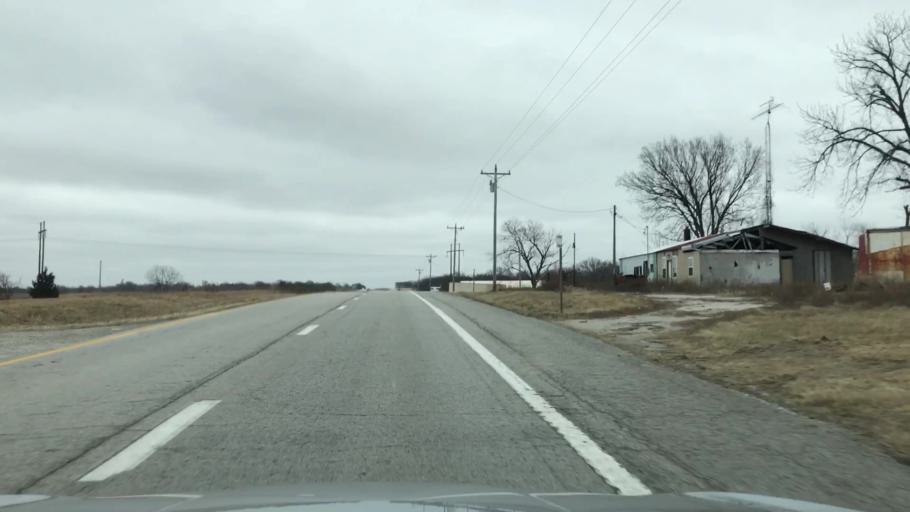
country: US
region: Missouri
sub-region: Linn County
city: Linneus
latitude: 39.7780
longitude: -93.1981
